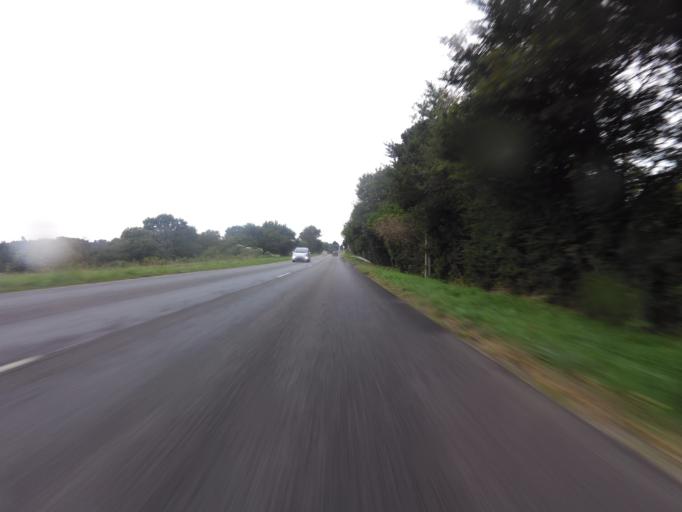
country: FR
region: Brittany
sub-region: Departement du Morbihan
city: Saint-Nolff
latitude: 47.6903
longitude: -2.6705
